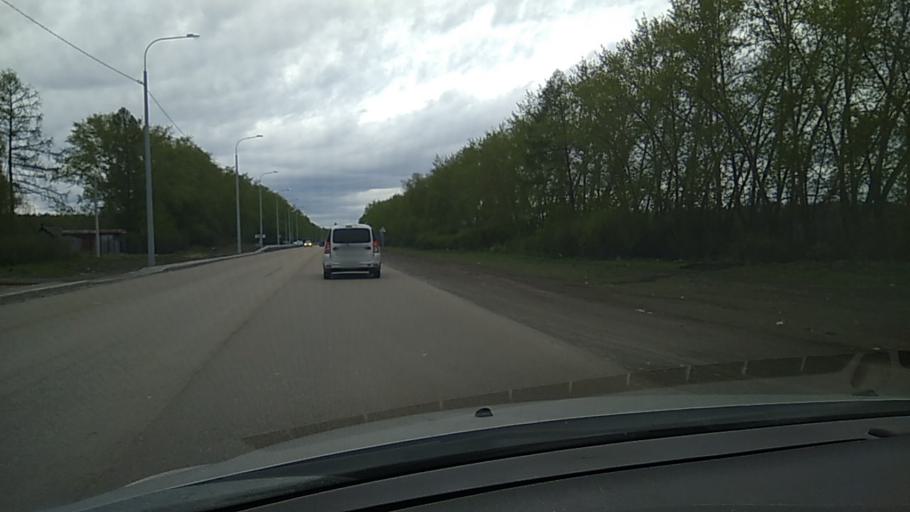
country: RU
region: Sverdlovsk
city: Dvurechensk
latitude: 56.6389
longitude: 61.2328
